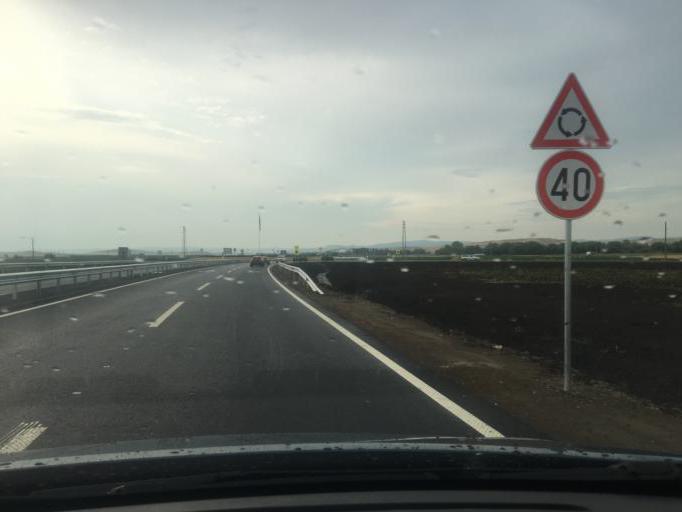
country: BG
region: Burgas
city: Aheloy
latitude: 42.6441
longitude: 27.6373
